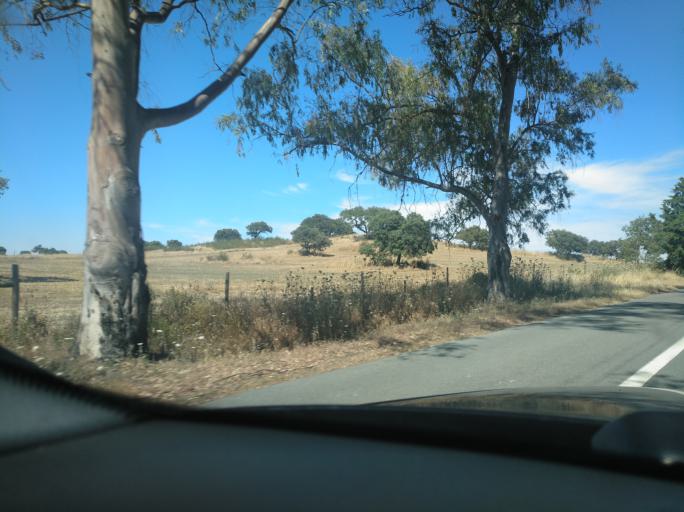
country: PT
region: Beja
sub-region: Almodovar
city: Almodovar
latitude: 37.5430
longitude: -7.9731
